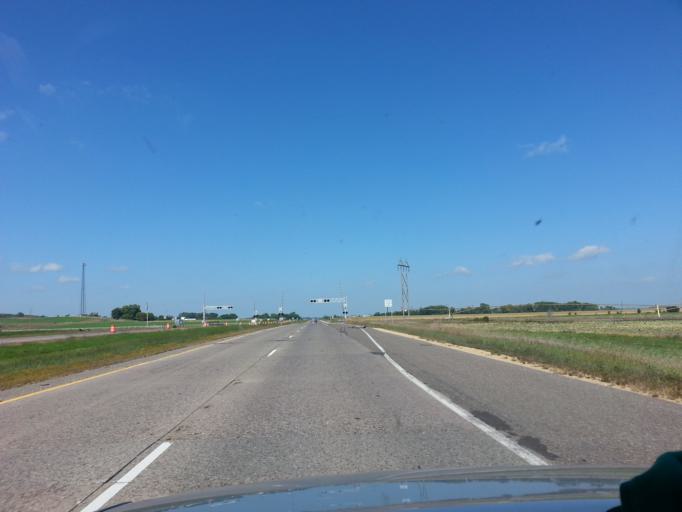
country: US
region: Minnesota
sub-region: Goodhue County
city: Cannon Falls
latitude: 44.5245
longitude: -92.9265
